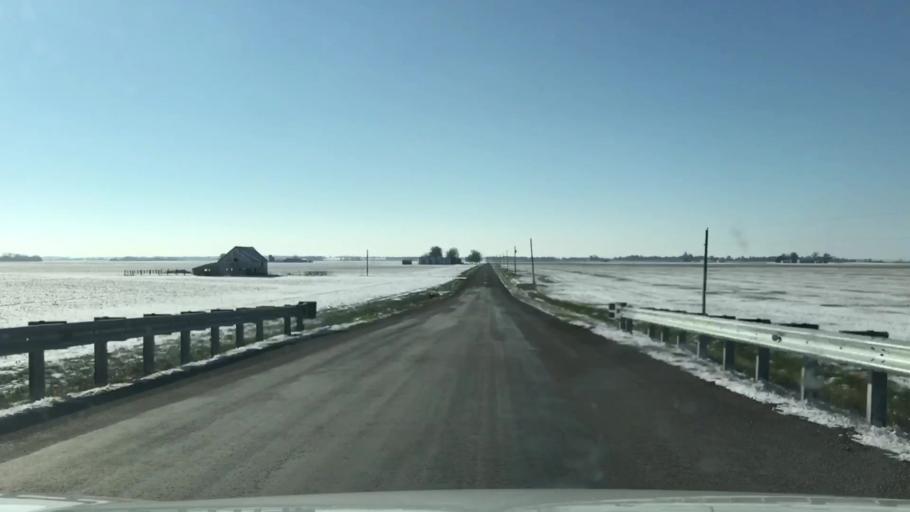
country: US
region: Illinois
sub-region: Washington County
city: Okawville
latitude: 38.4261
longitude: -89.4777
